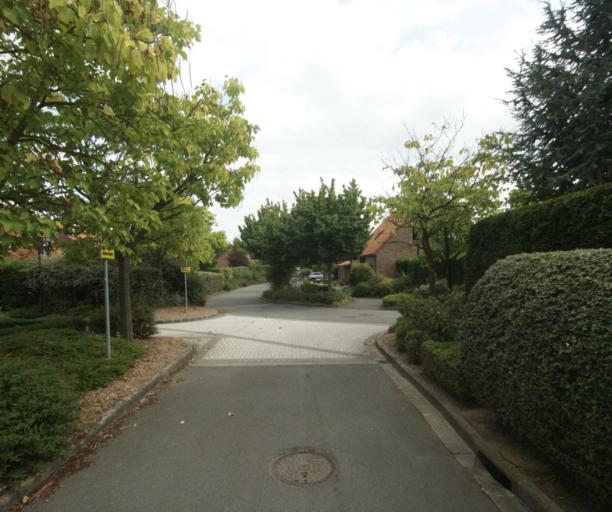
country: FR
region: Nord-Pas-de-Calais
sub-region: Departement du Nord
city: Tressin
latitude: 50.6138
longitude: 3.1919
